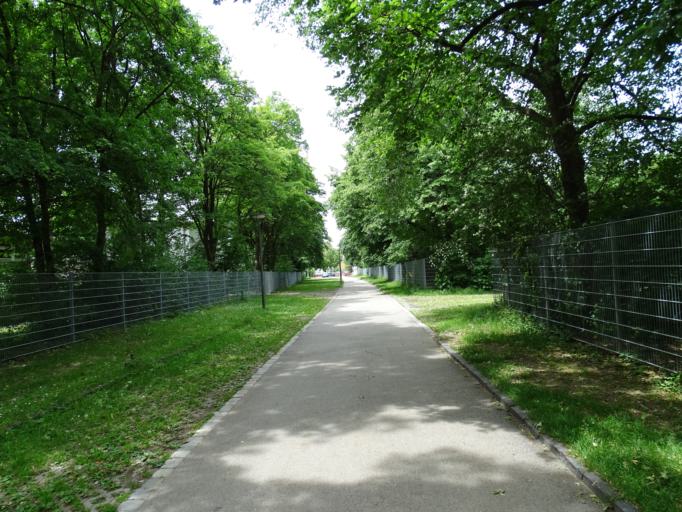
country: DE
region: Bavaria
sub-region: Upper Bavaria
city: Oberschleissheim
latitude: 48.2079
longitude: 11.5696
